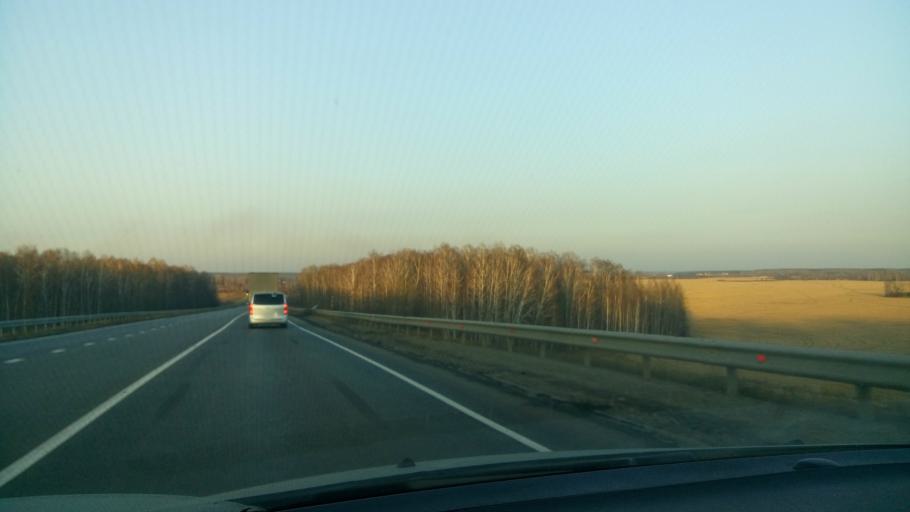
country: RU
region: Sverdlovsk
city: Yelanskiy
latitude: 56.7957
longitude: 62.5139
